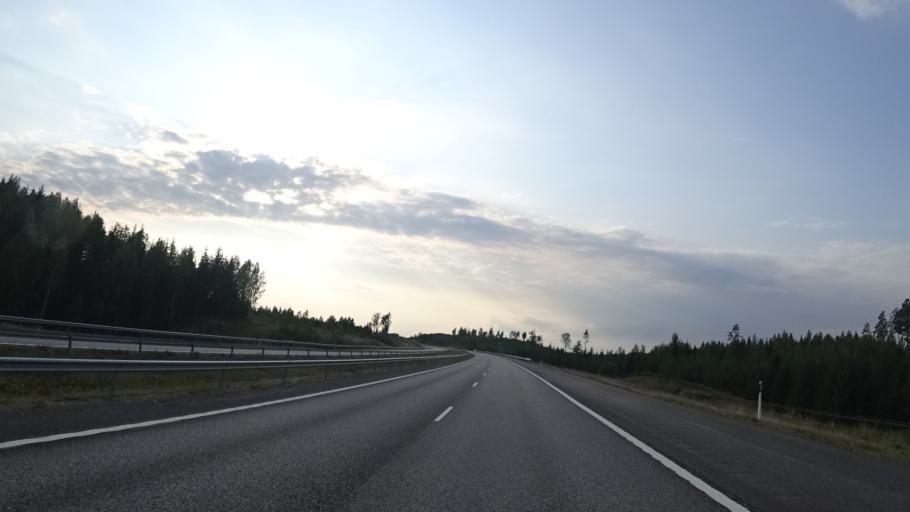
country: FI
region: Uusimaa
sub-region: Loviisa
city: Perna
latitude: 60.4891
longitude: 26.0051
